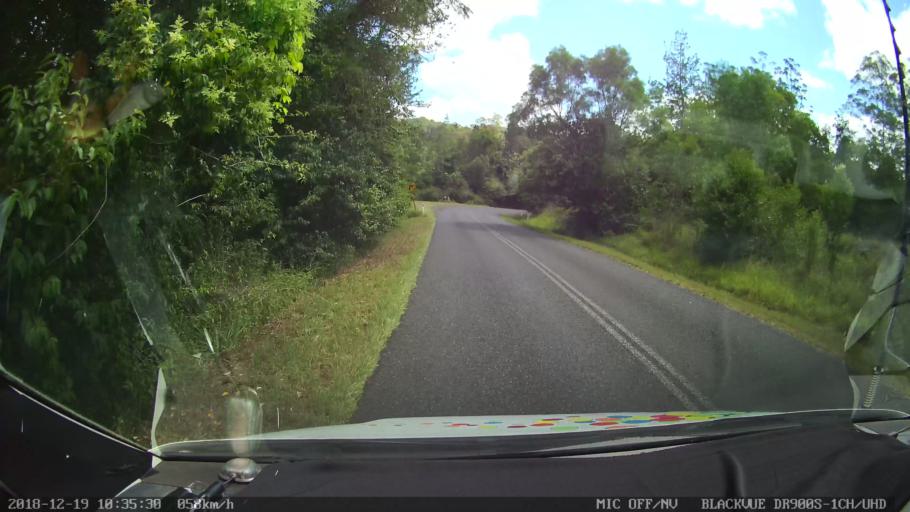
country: AU
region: New South Wales
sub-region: Lismore Municipality
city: Larnook
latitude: -28.5758
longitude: 153.1365
